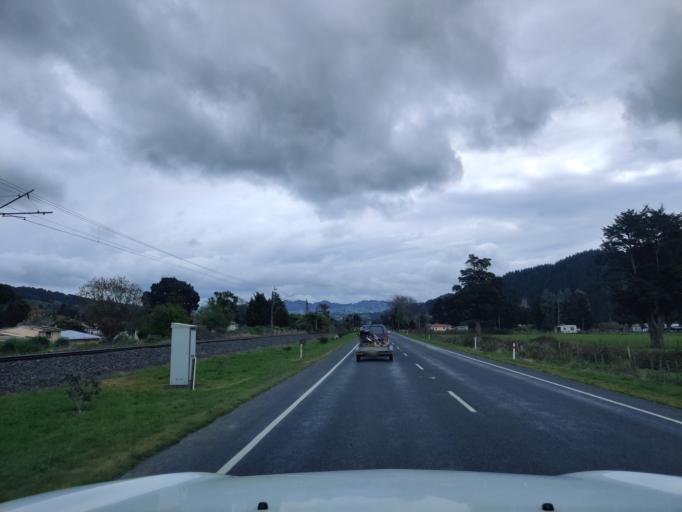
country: NZ
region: Waikato
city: Turangi
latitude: -38.8814
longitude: 175.2935
